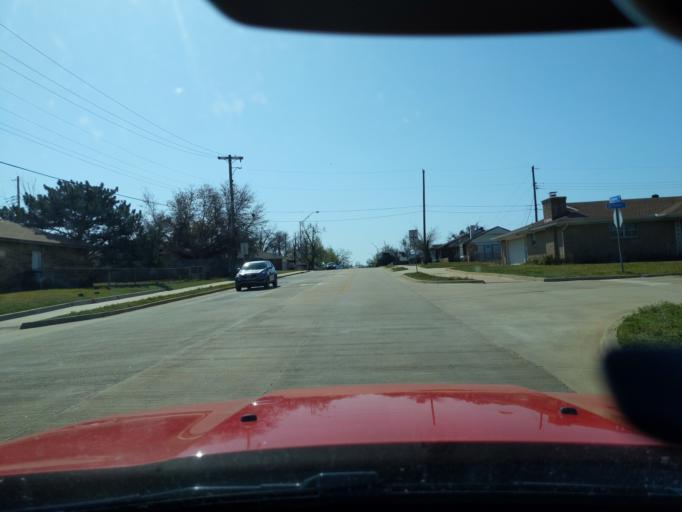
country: US
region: Oklahoma
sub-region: Cleveland County
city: Moore
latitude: 35.3475
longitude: -97.4898
